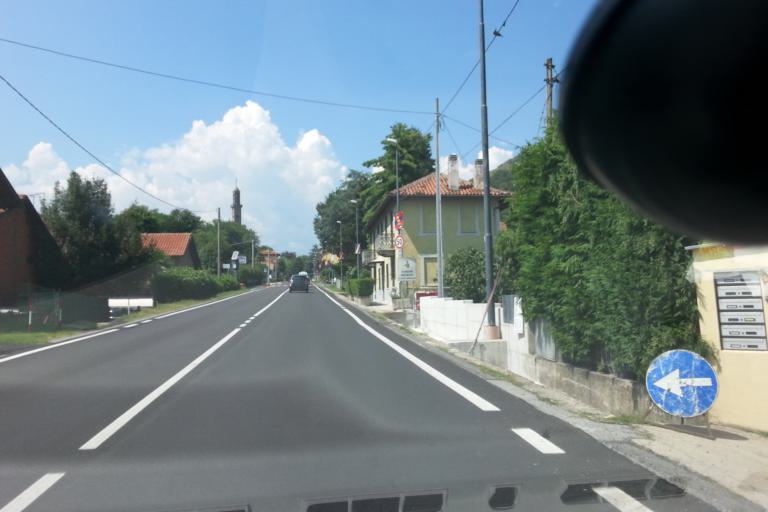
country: IT
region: Piedmont
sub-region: Provincia di Torino
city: Trana
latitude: 45.0388
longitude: 7.4186
